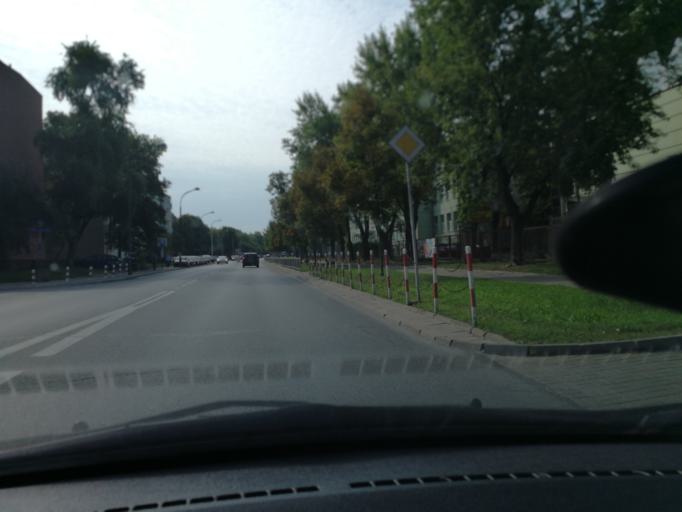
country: PL
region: Masovian Voivodeship
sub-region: Warszawa
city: Bemowo
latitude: 52.2344
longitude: 20.9406
